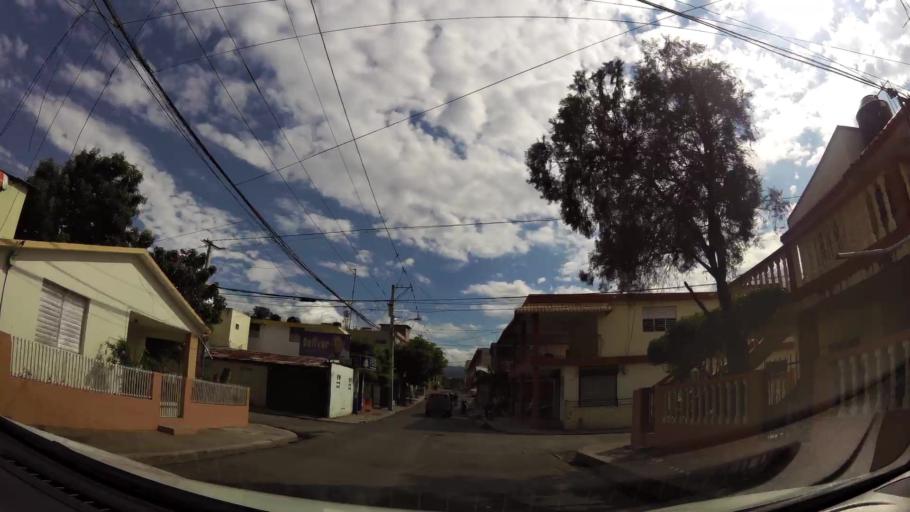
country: DO
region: La Vega
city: Concepcion de La Vega
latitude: 19.2269
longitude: -70.5253
